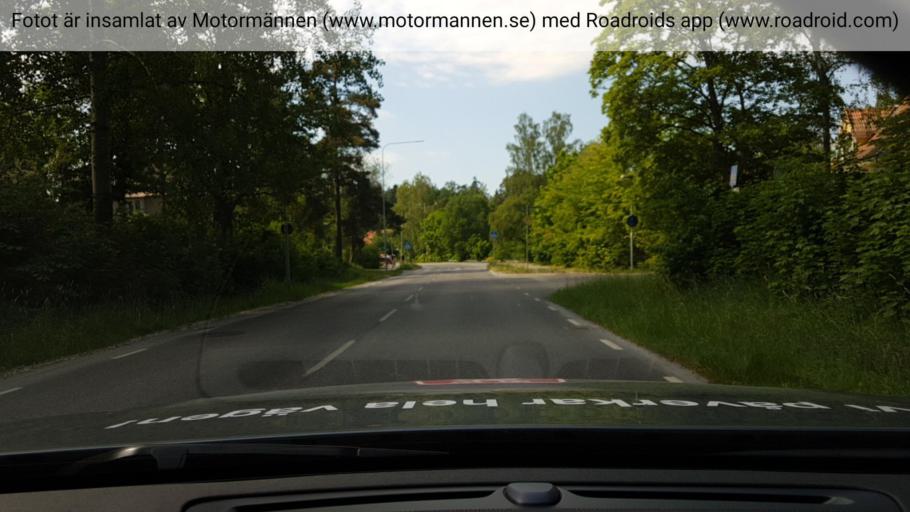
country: SE
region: Stockholm
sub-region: Lidingo
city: Lidingoe
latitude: 59.3696
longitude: 18.1305
